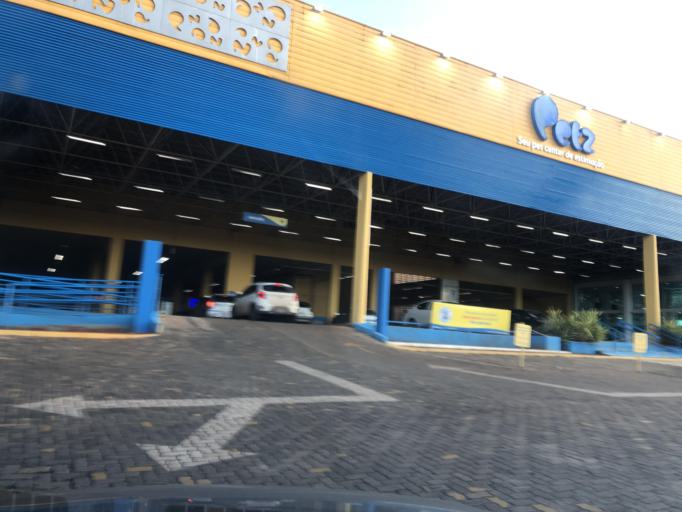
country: BR
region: Federal District
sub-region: Brasilia
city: Brasilia
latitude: -15.7357
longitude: -47.9025
